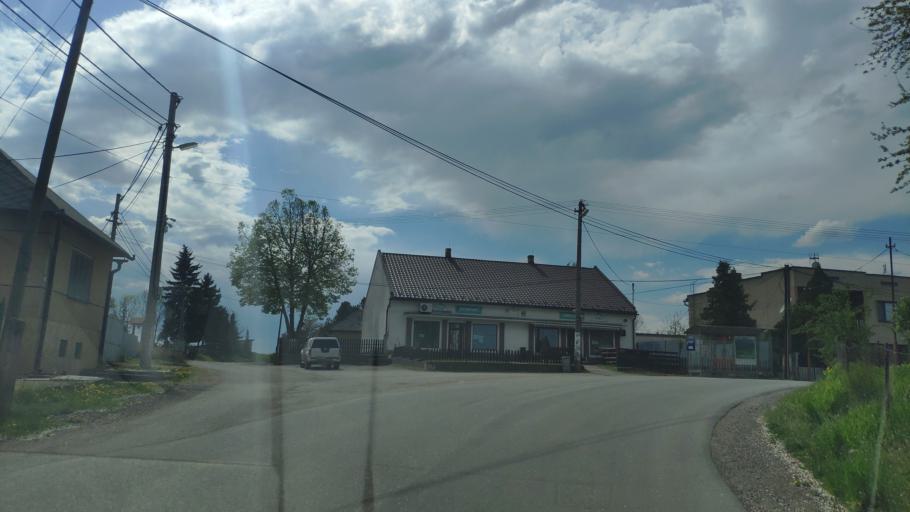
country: SK
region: Kosicky
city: Moldava nad Bodvou
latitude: 48.5816
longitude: 20.9235
